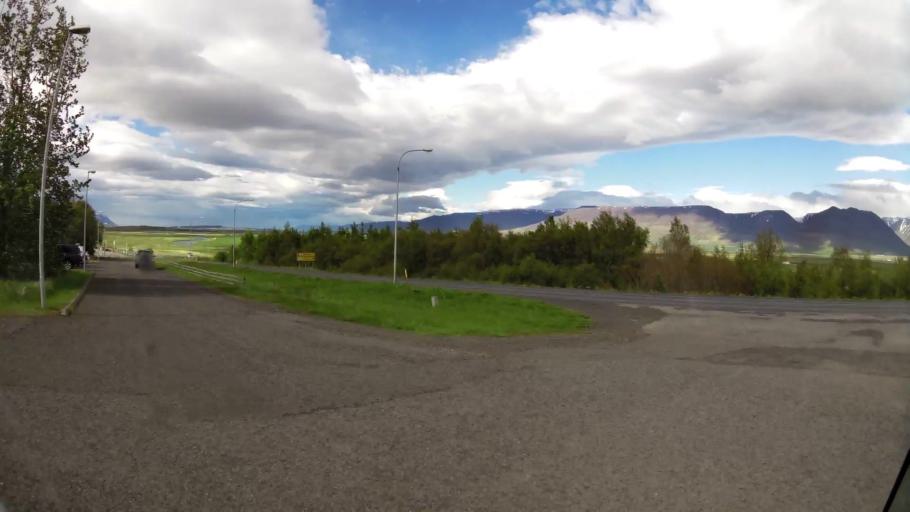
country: IS
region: Northwest
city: Saudarkrokur
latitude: 65.5510
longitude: -19.4436
